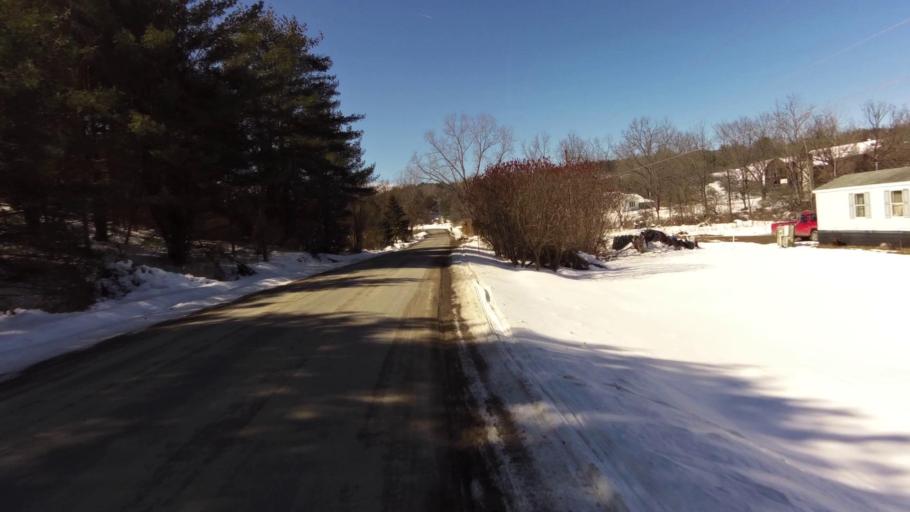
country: US
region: New York
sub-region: Allegany County
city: Houghton
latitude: 42.3605
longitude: -78.1476
